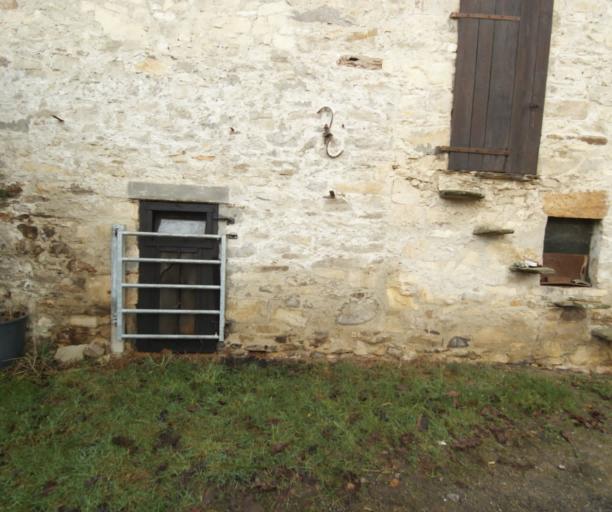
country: FR
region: Limousin
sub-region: Departement de la Correze
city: Chameyrat
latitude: 45.2268
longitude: 1.7173
